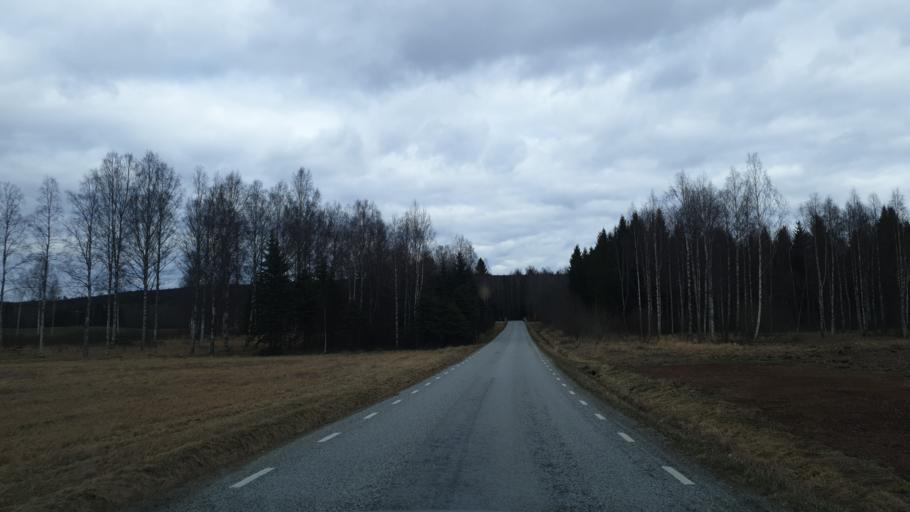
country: SE
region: OErebro
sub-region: Nora Kommun
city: As
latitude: 59.6284
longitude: 14.9342
